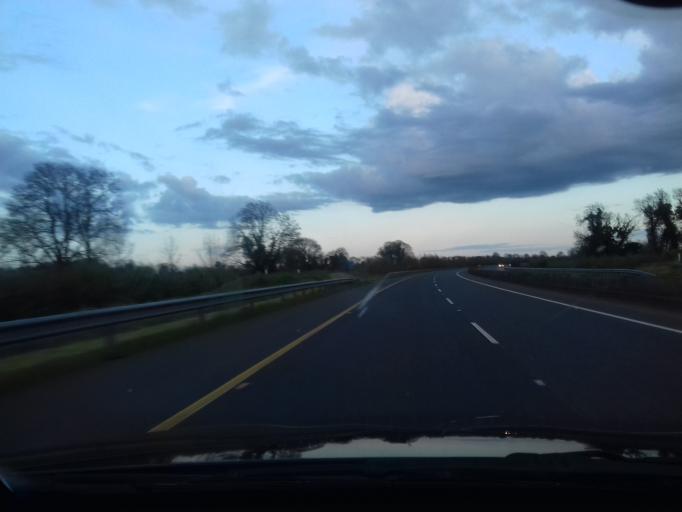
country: IE
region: Leinster
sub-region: An Mhi
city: Kells
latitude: 53.6883
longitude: -6.8106
